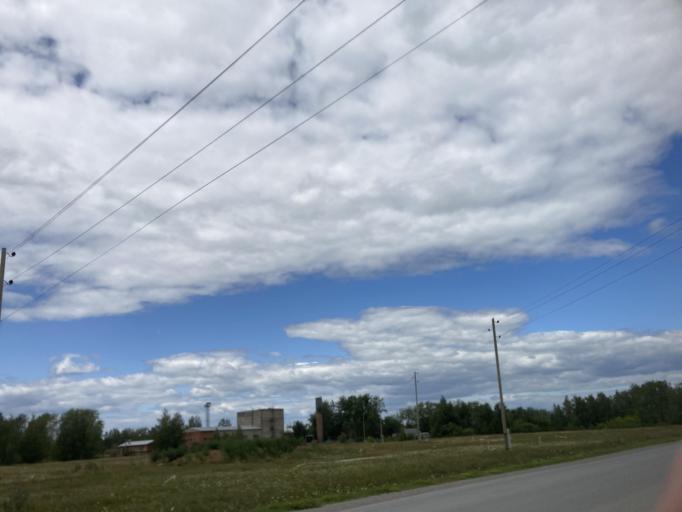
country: RU
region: Sverdlovsk
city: Bogdanovich
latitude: 56.7927
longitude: 62.0679
